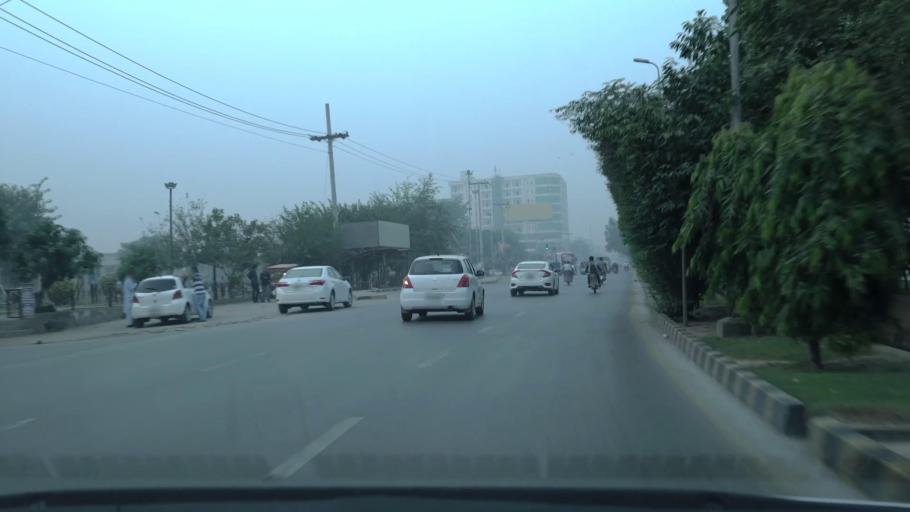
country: PK
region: Punjab
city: Lahore
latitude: 31.4718
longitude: 74.3029
